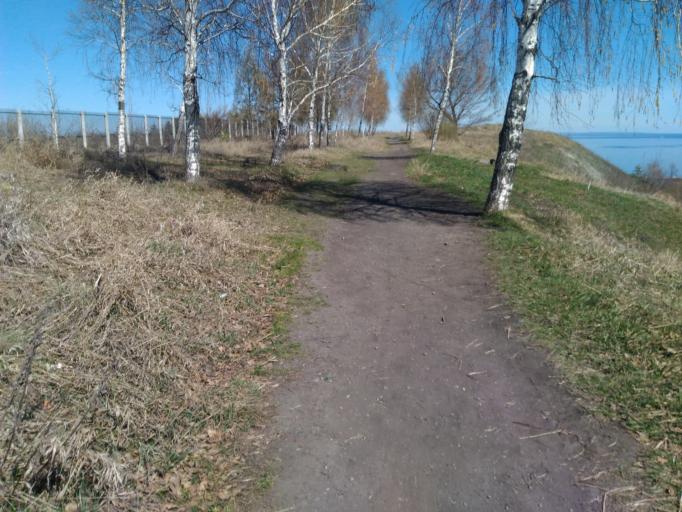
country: RU
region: Ulyanovsk
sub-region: Ulyanovskiy Rayon
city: Ulyanovsk
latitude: 54.3510
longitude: 48.3927
